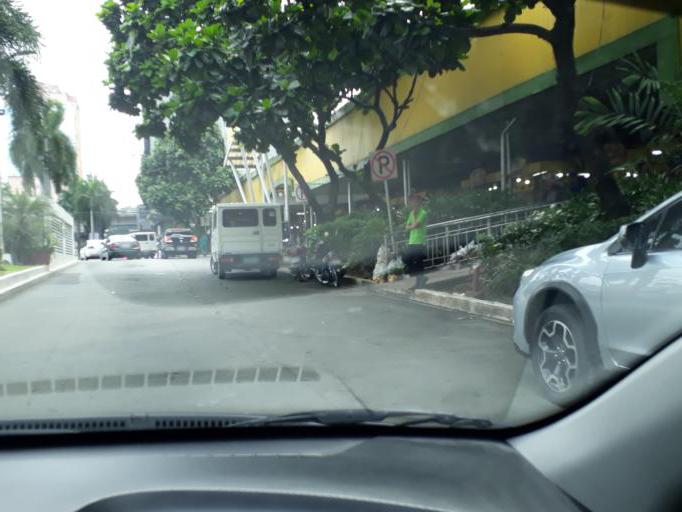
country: PH
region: Metro Manila
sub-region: San Juan
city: San Juan
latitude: 14.6190
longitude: 121.0530
